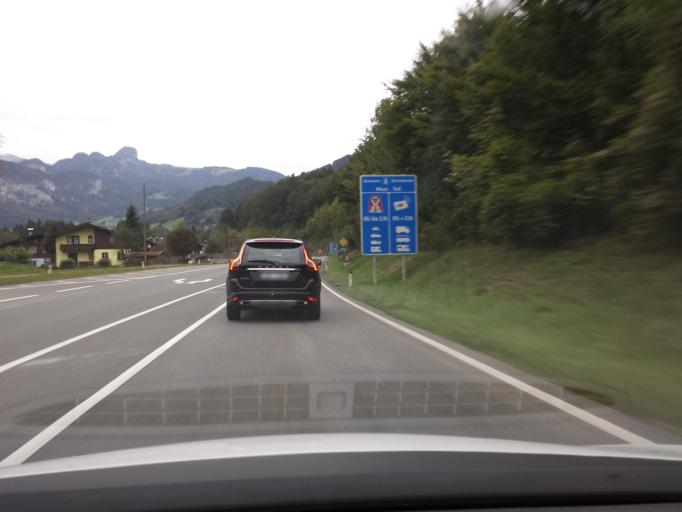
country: AT
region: Salzburg
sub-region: Politischer Bezirk Zell am See
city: Unken
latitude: 47.6646
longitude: 12.7508
